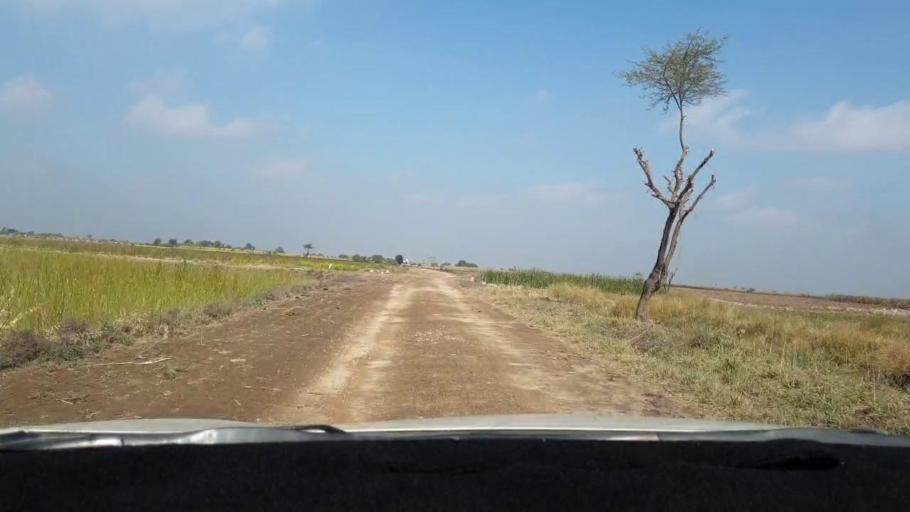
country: PK
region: Sindh
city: Berani
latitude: 25.7456
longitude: 69.0077
